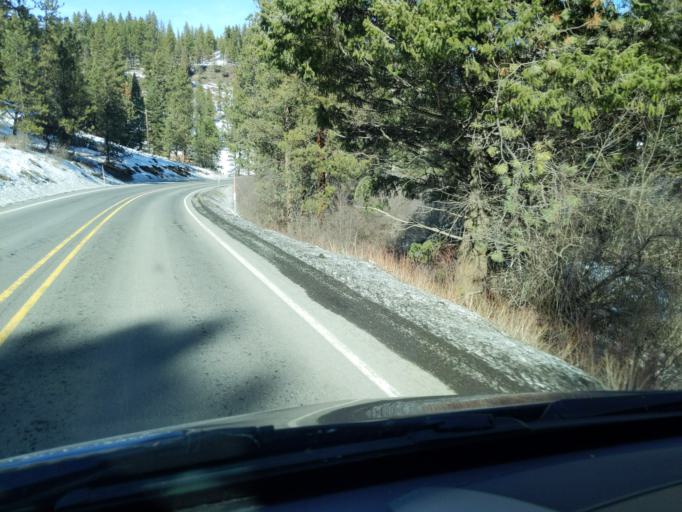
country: US
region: Oregon
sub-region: Grant County
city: John Day
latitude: 44.9379
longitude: -119.0084
